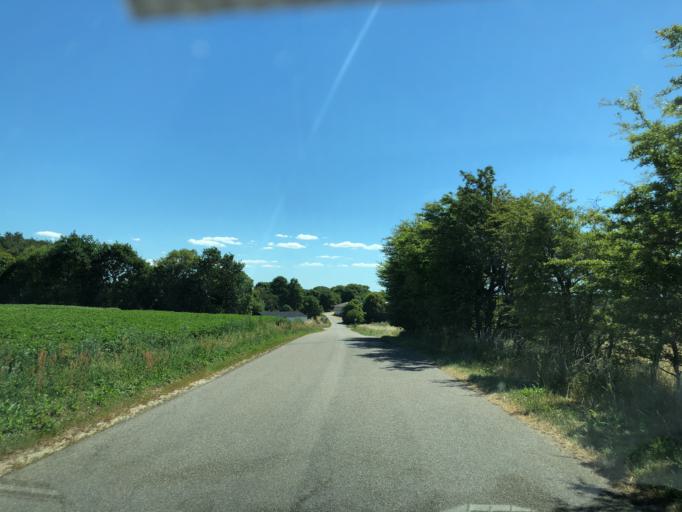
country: DK
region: Central Jutland
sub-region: Viborg Kommune
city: Viborg
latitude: 56.5569
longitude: 9.4224
